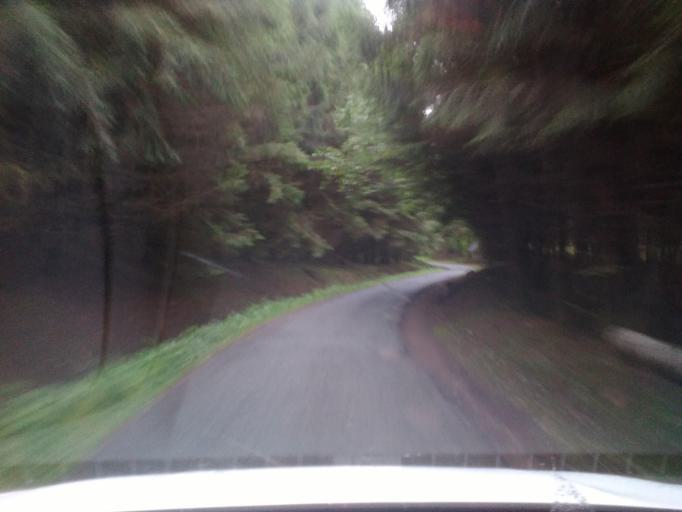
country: FR
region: Lorraine
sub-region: Departement des Vosges
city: Moyenmoutier
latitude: 48.3753
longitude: 6.9398
